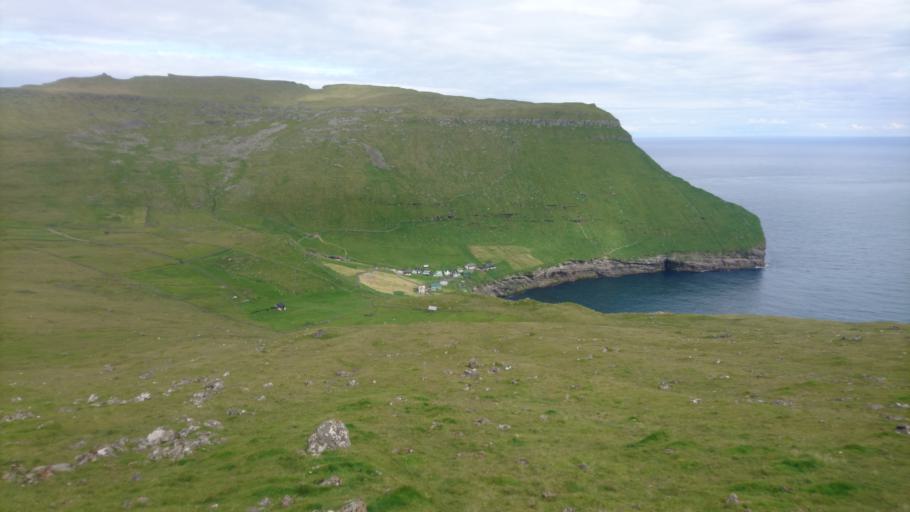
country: FO
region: Nordoyar
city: Klaksvik
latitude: 62.3259
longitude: -6.2877
